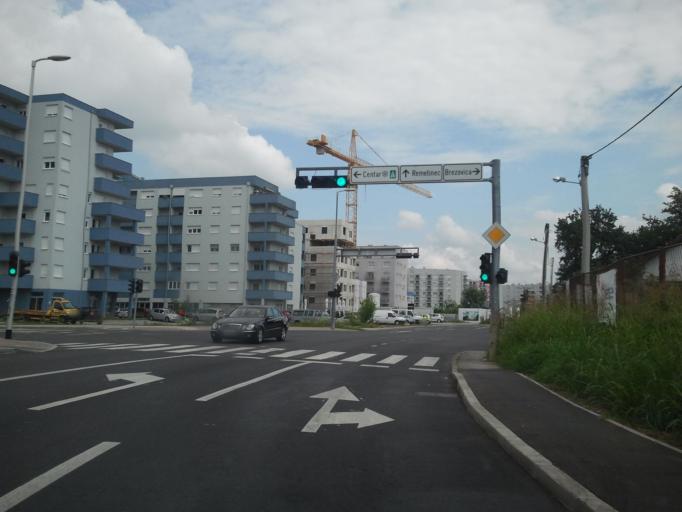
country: HR
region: Grad Zagreb
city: Zadvorsko
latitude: 45.7676
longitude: 15.9346
